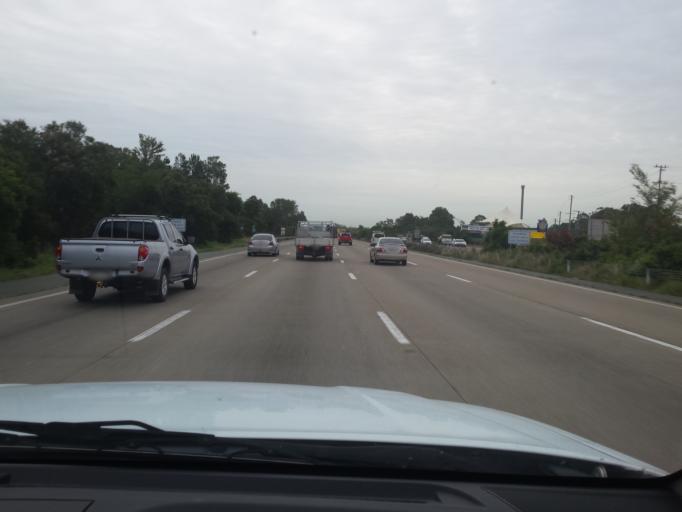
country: AU
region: Queensland
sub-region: Gold Coast
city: Oxenford
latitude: -27.8738
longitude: 153.3137
